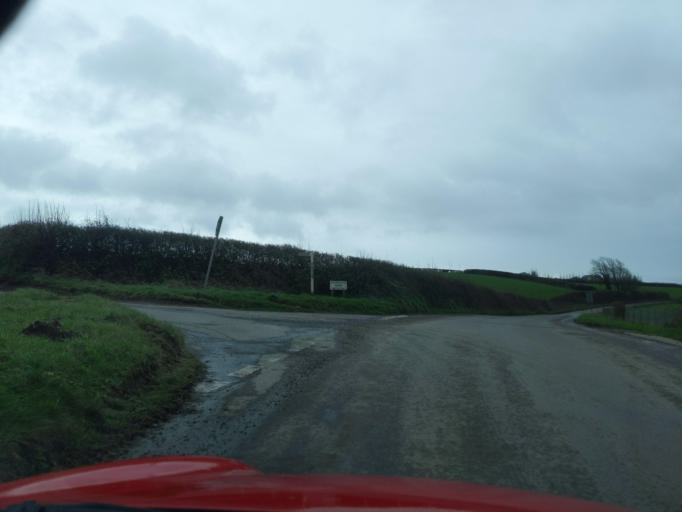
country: GB
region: England
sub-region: Devon
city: Modbury
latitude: 50.3354
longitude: -3.8688
